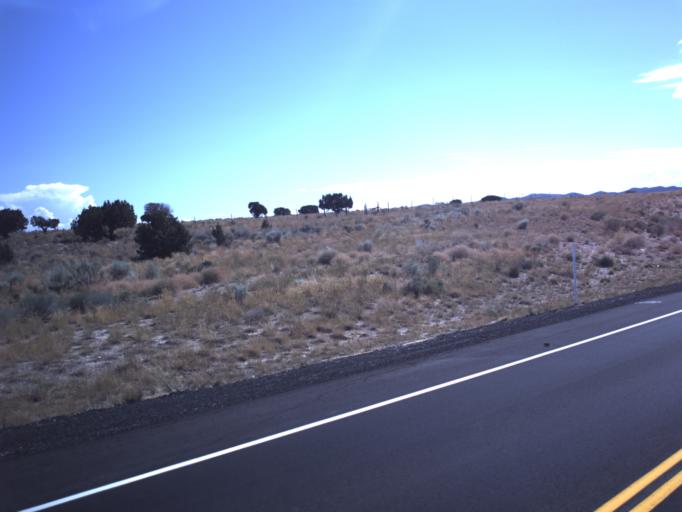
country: US
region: Utah
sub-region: Utah County
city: Eagle Mountain
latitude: 40.0691
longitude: -112.3289
